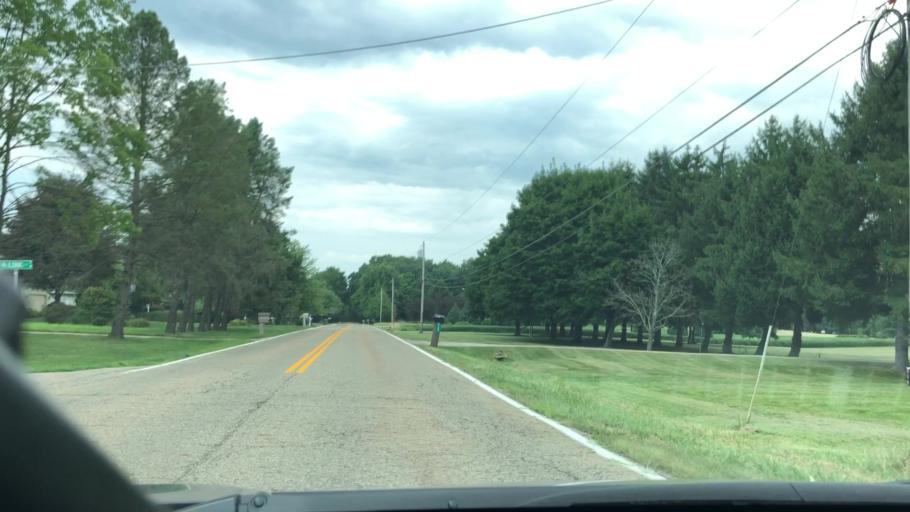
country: US
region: Ohio
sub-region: Summit County
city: New Franklin
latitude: 40.8981
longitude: -81.5177
